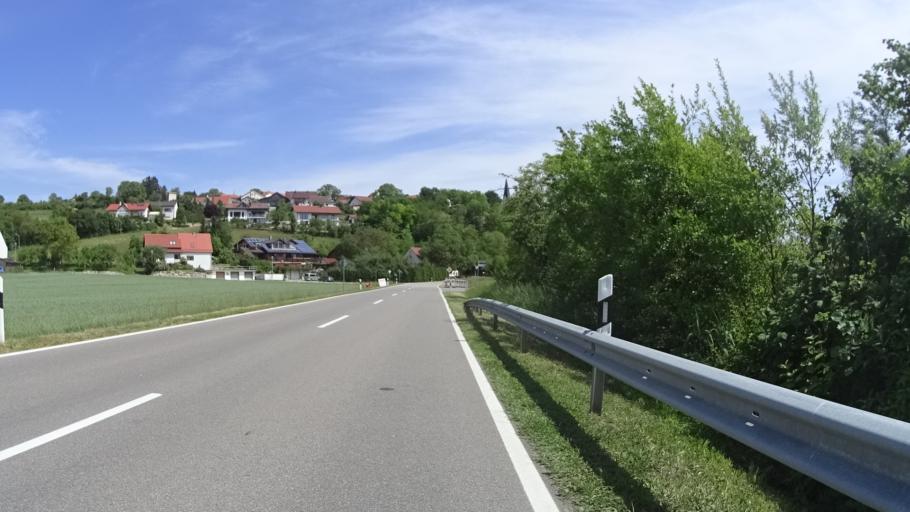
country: DE
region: Bavaria
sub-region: Lower Bavaria
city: Teugn
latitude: 48.9284
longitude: 11.9804
